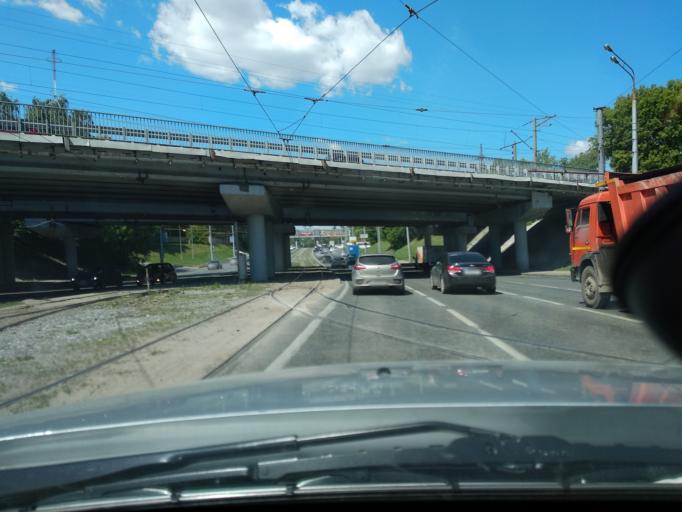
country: RU
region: Tatarstan
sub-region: Gorod Kazan'
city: Kazan
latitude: 55.8166
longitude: 49.1802
